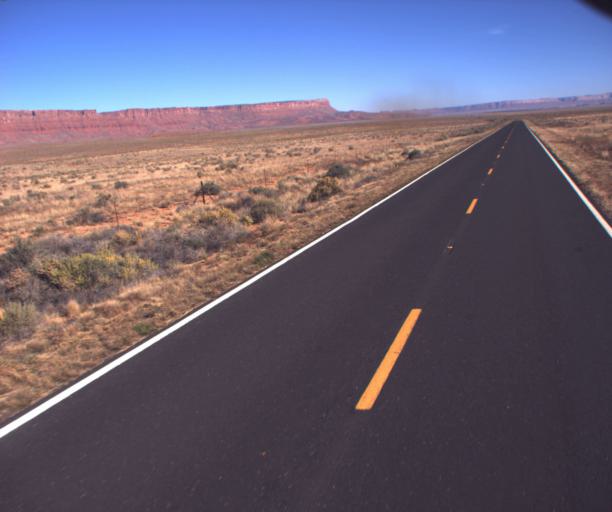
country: US
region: Arizona
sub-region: Coconino County
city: Fredonia
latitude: 36.7197
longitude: -112.0085
